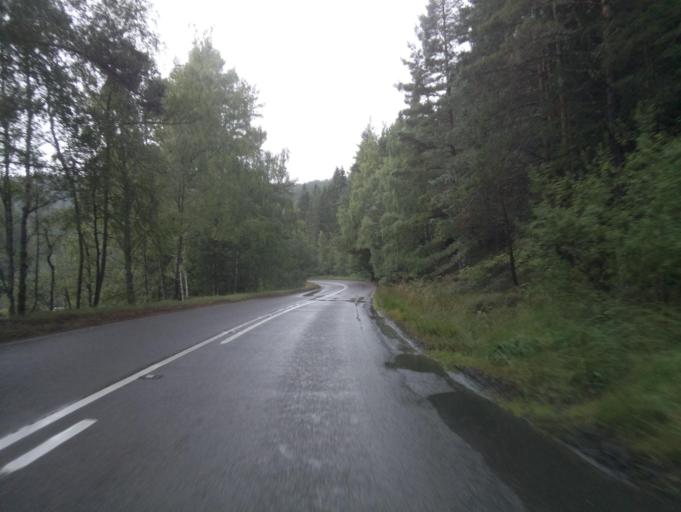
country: GB
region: Scotland
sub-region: Aberdeenshire
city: Ballater
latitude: 57.0174
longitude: -3.2931
